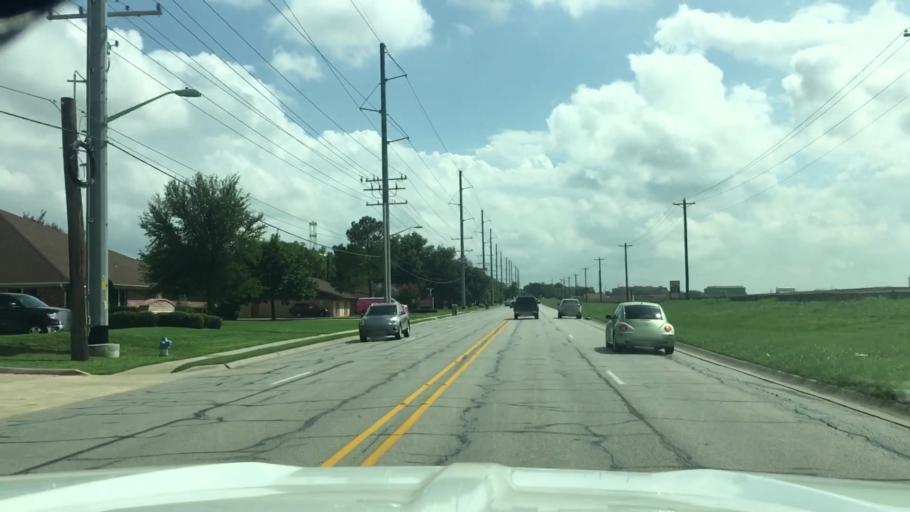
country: US
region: Texas
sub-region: Denton County
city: Denton
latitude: 33.2265
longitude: -97.1611
